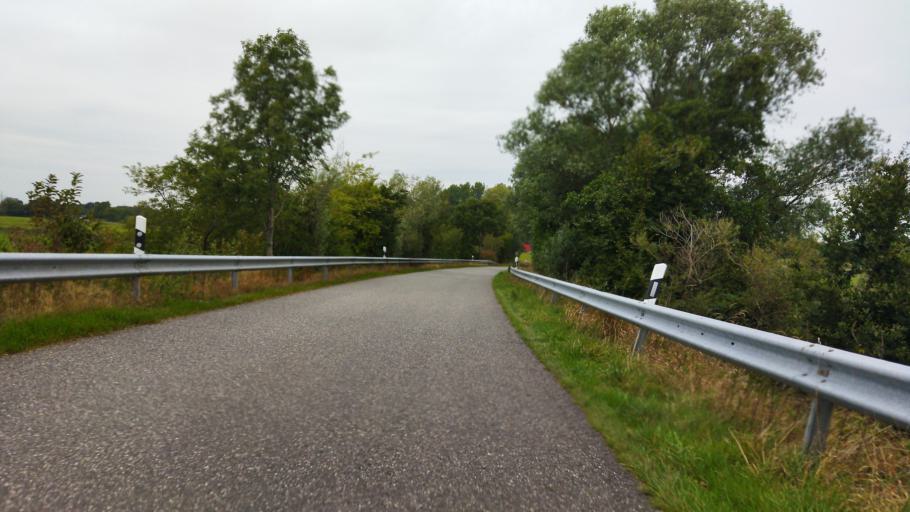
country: DE
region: Lower Saxony
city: Leer
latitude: 53.2566
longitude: 7.4376
